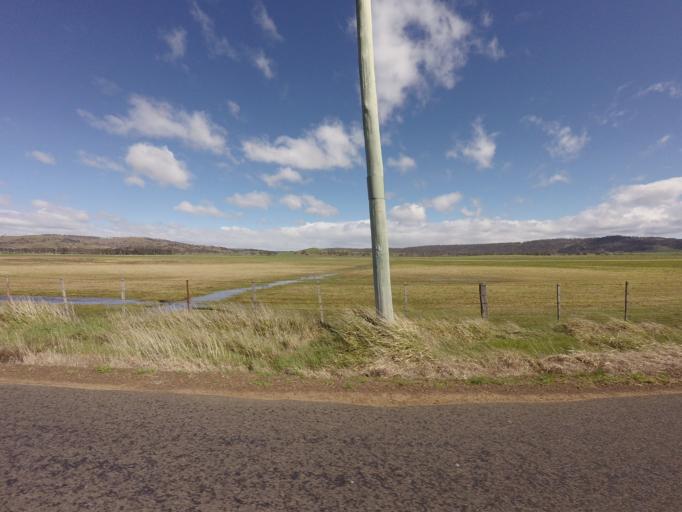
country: AU
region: Tasmania
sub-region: Northern Midlands
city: Evandale
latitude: -42.0185
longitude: 147.4668
